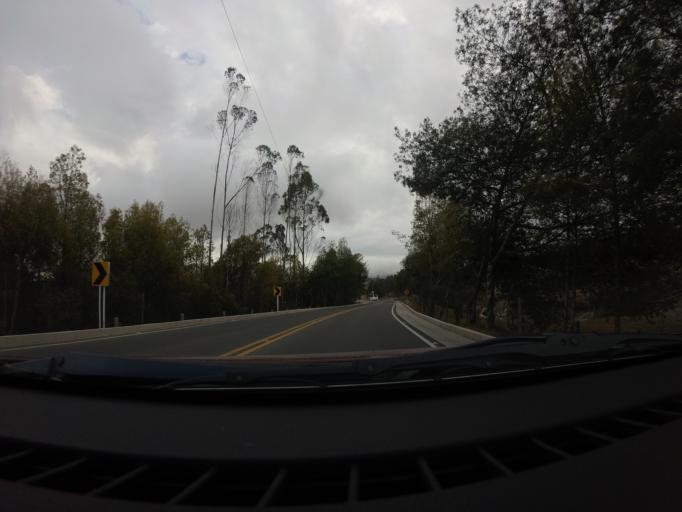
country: CO
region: Boyaca
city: Tunja
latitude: 5.5566
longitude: -73.4083
